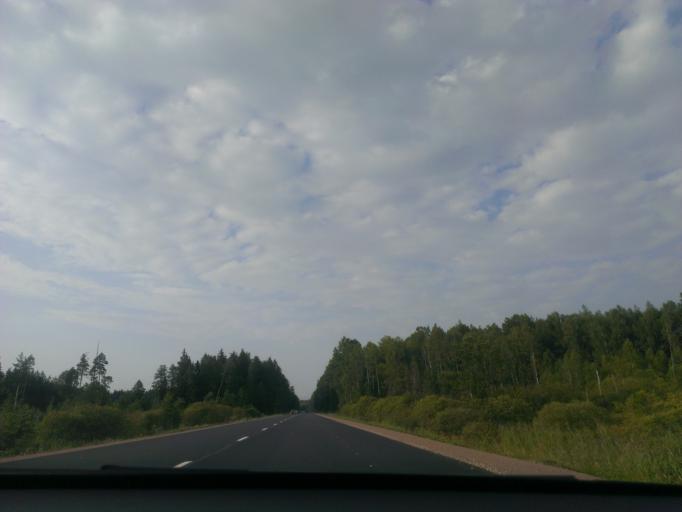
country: LV
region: Lecava
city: Iecava
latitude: 56.7044
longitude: 24.2451
